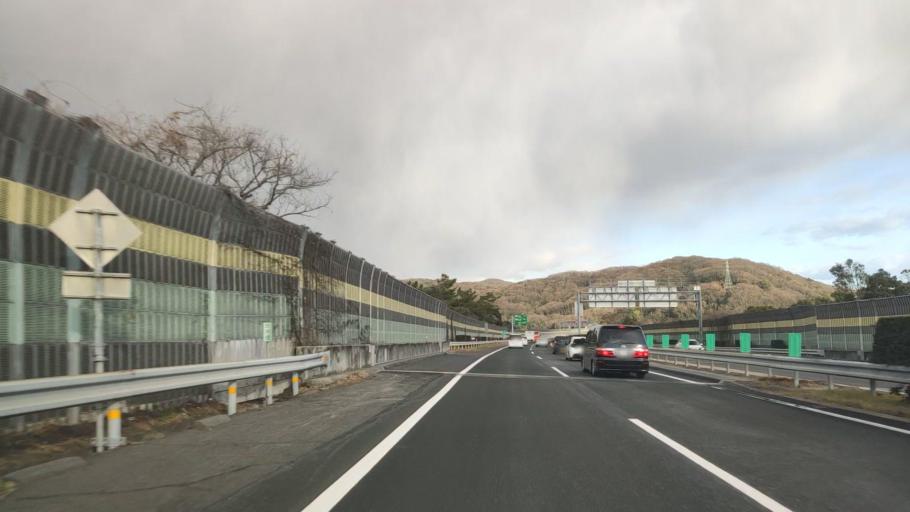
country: JP
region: Okayama
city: Soja
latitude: 34.6796
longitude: 133.8243
